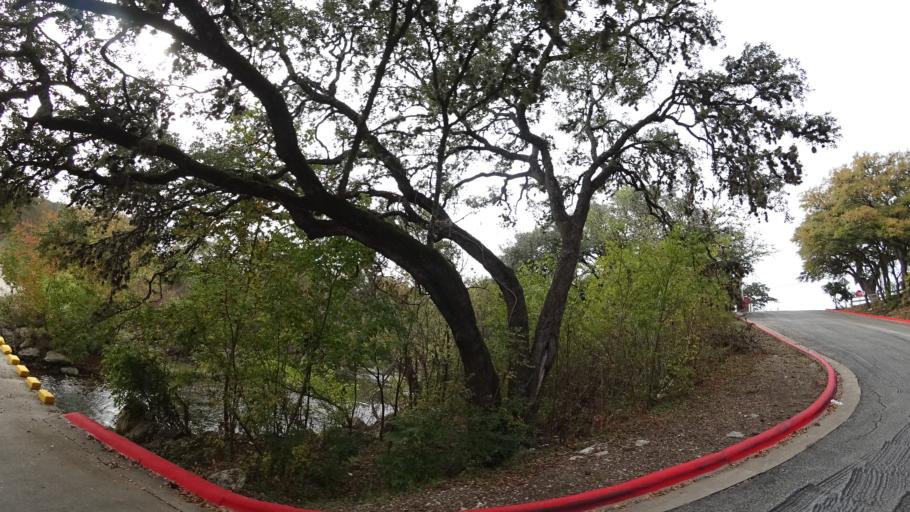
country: US
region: Texas
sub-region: Williamson County
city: Round Rock
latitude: 30.5168
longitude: -97.6623
